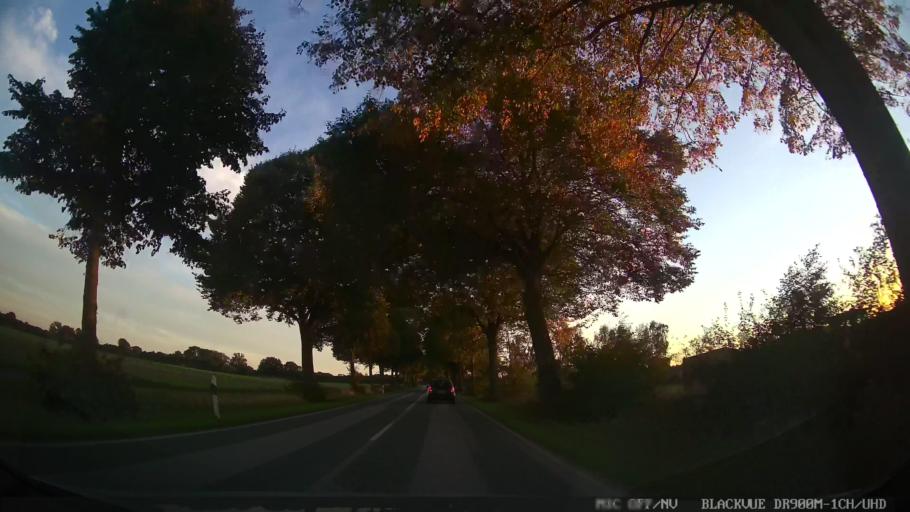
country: DE
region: Schleswig-Holstein
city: Susel
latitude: 54.0555
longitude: 10.6827
